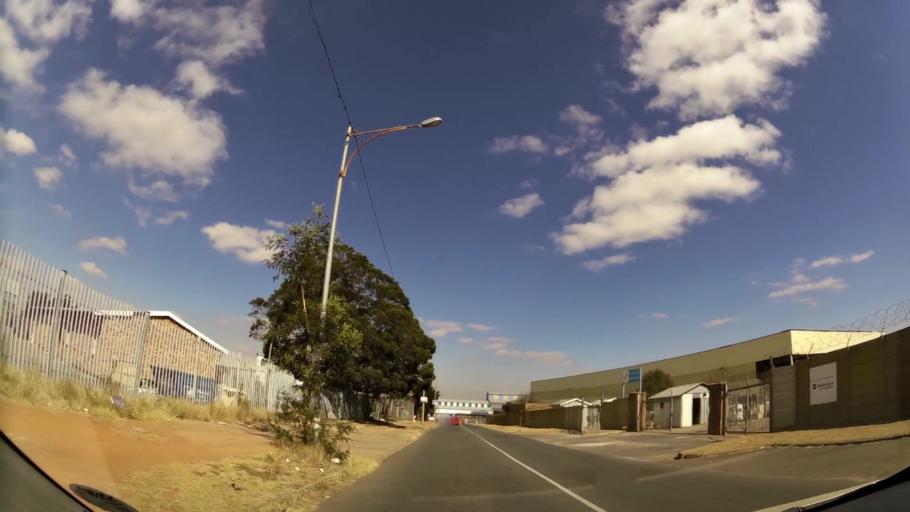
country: ZA
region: Gauteng
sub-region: West Rand District Municipality
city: Krugersdorp
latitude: -26.1138
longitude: 27.8099
